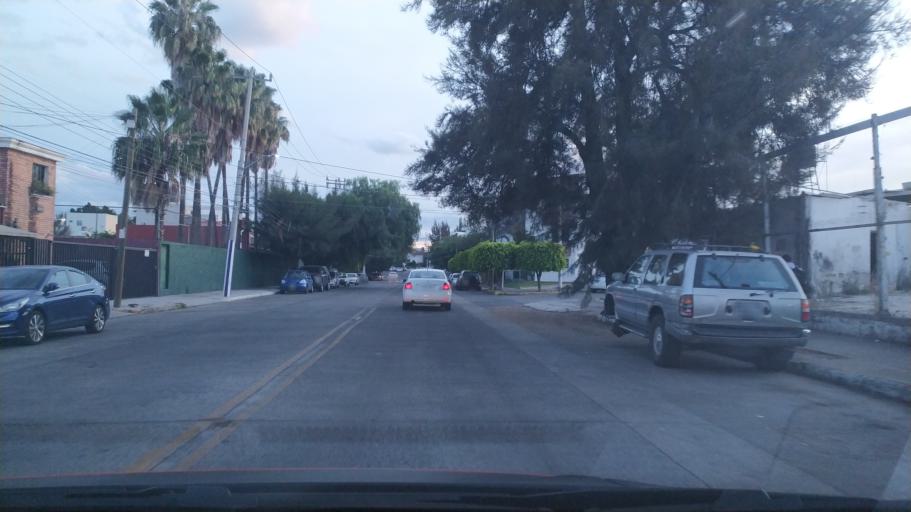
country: MX
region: Jalisco
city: Guadalajara
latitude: 20.6421
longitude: -103.4124
